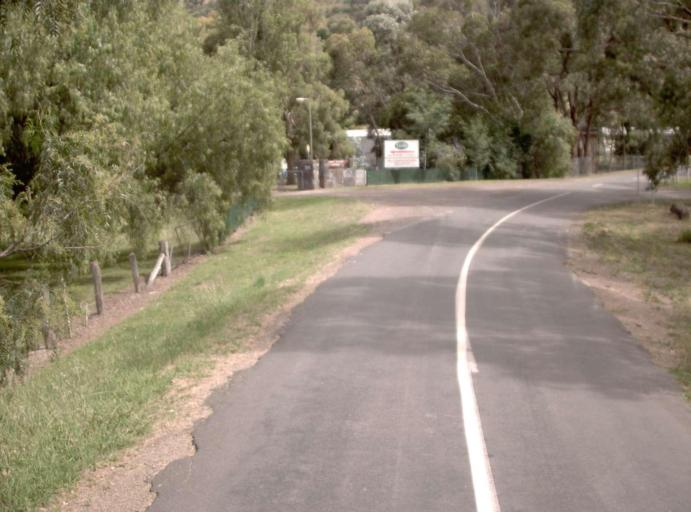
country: AU
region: Victoria
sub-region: Wellington
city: Heyfield
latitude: -37.6287
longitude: 146.6229
